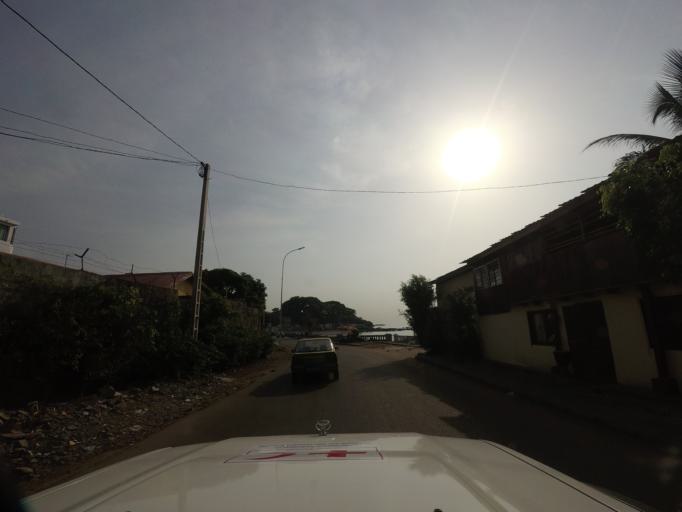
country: GN
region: Conakry
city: Camayenne
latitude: 9.5161
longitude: -13.6965
